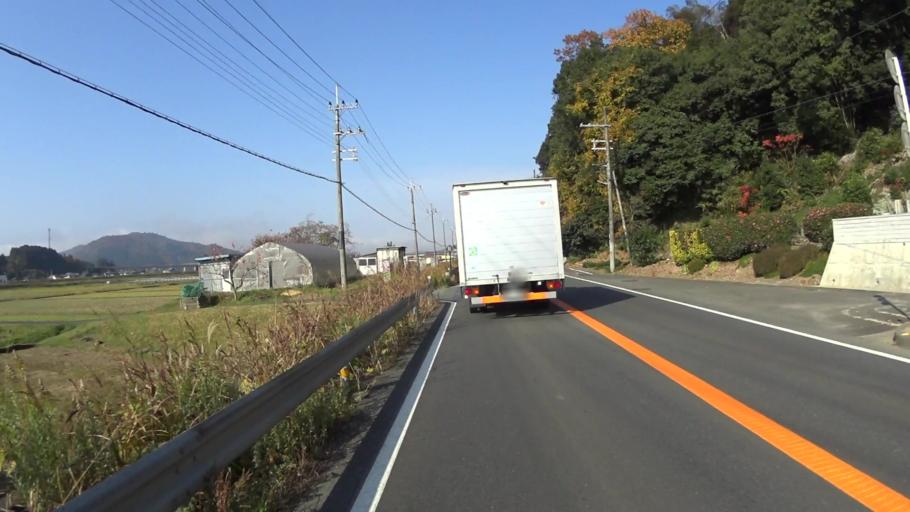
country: JP
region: Kyoto
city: Ayabe
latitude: 35.2611
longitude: 135.1916
